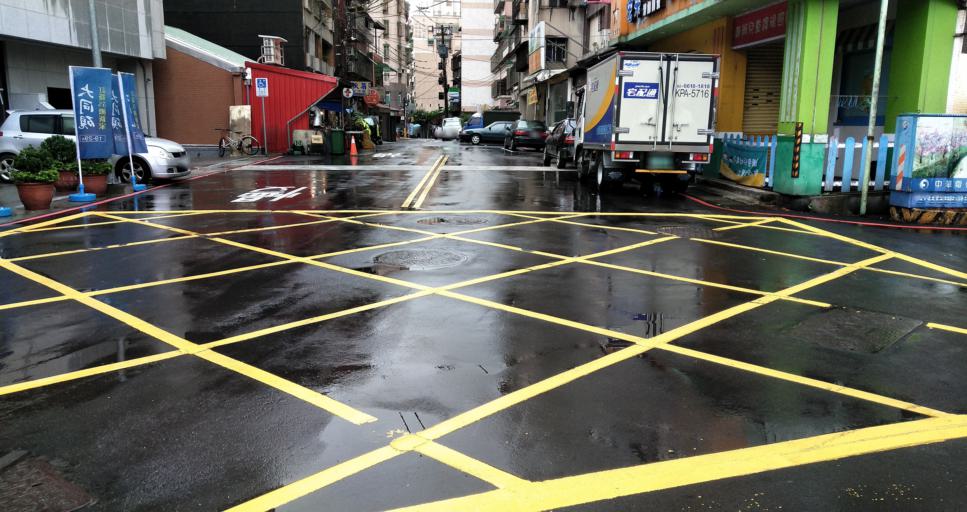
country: TW
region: Taiwan
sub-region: Keelung
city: Keelung
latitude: 25.0707
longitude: 121.6634
